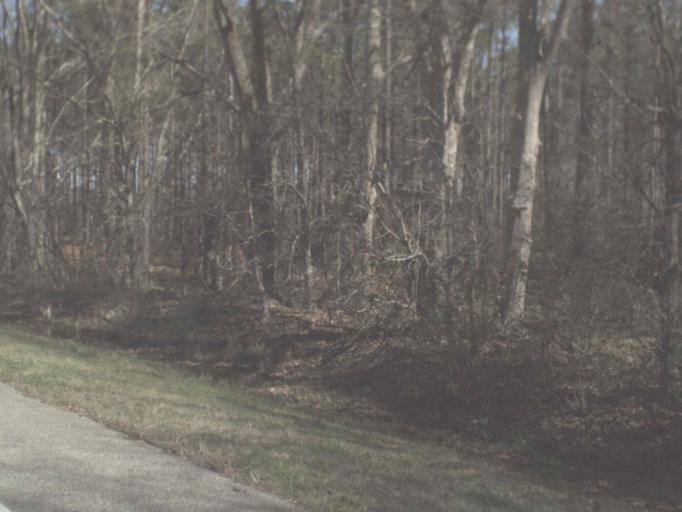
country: US
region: Florida
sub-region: Calhoun County
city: Blountstown
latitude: 30.5777
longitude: -85.0218
